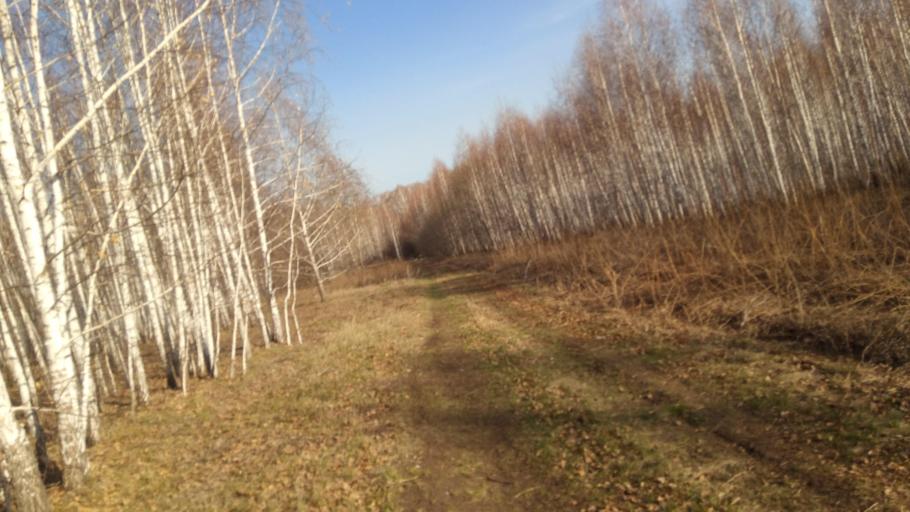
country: RU
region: Chelyabinsk
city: Sargazy
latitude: 55.1156
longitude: 61.2398
